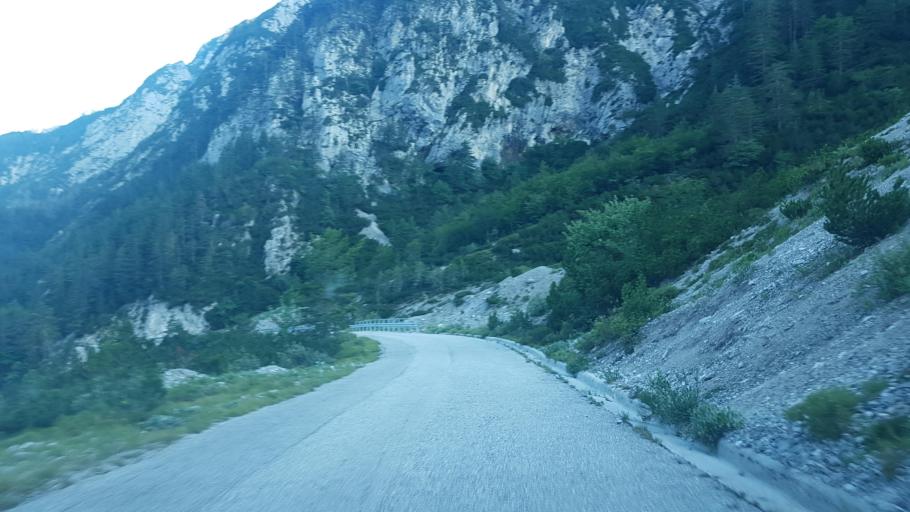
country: IT
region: Friuli Venezia Giulia
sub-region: Provincia di Udine
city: Malborghetto
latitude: 46.4632
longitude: 13.4342
